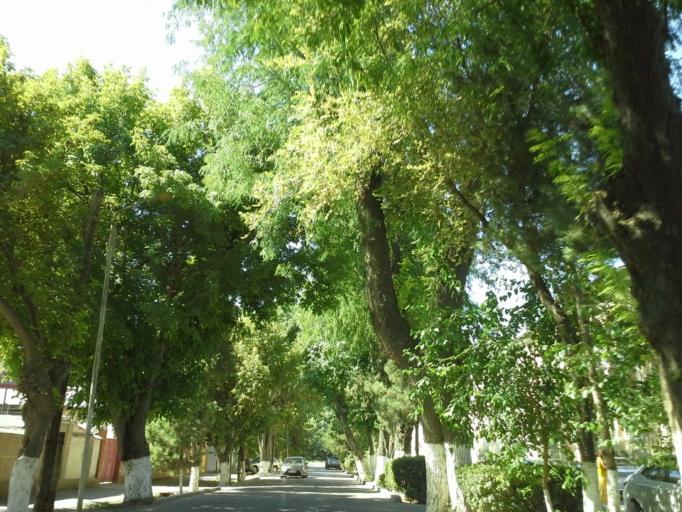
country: TM
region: Ahal
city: Ashgabat
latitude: 37.9477
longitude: 58.3559
